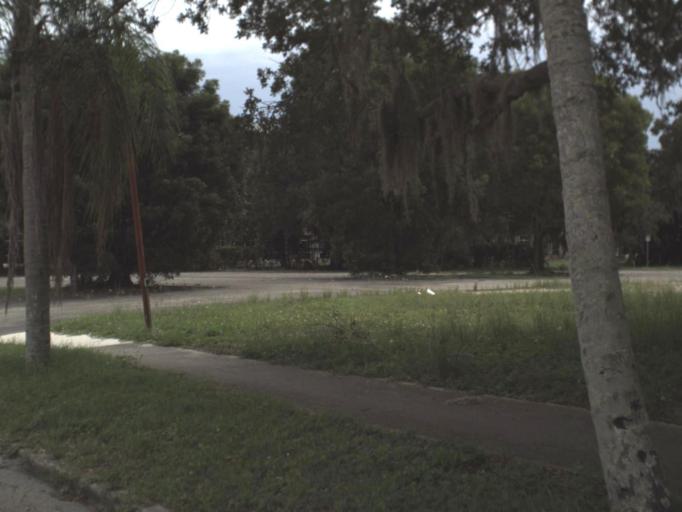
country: US
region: Florida
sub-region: Lee County
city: North Fort Myers
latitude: 26.6385
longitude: -81.8683
